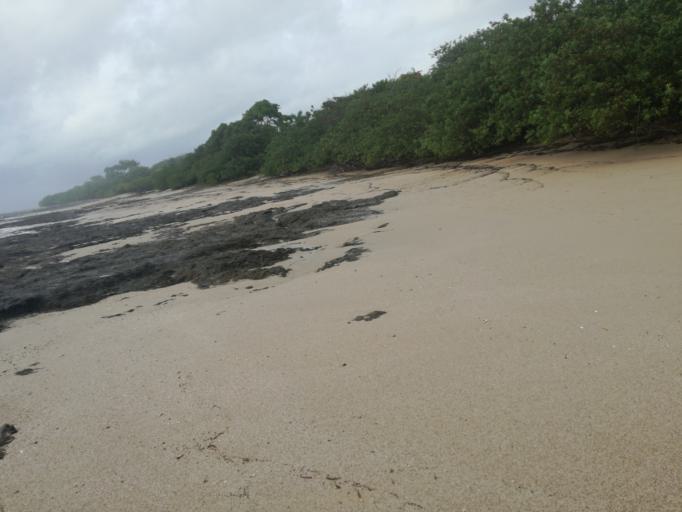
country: CR
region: Guanacaste
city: Santa Cruz
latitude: 10.2868
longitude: -85.8516
